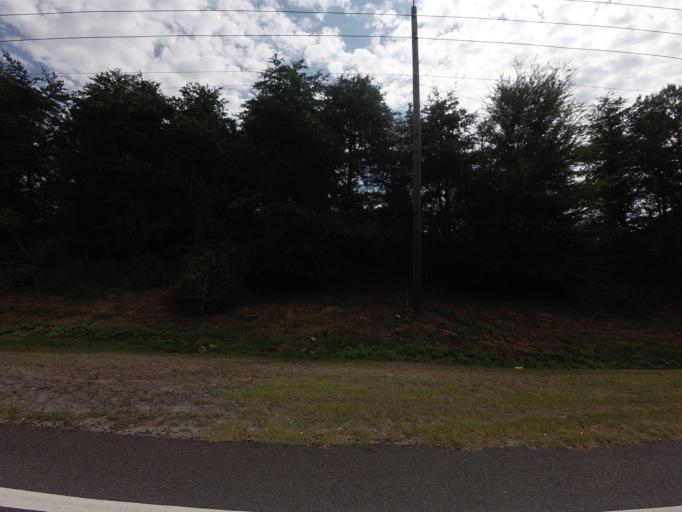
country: US
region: Georgia
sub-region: Fulton County
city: Johns Creek
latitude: 34.0335
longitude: -84.1702
